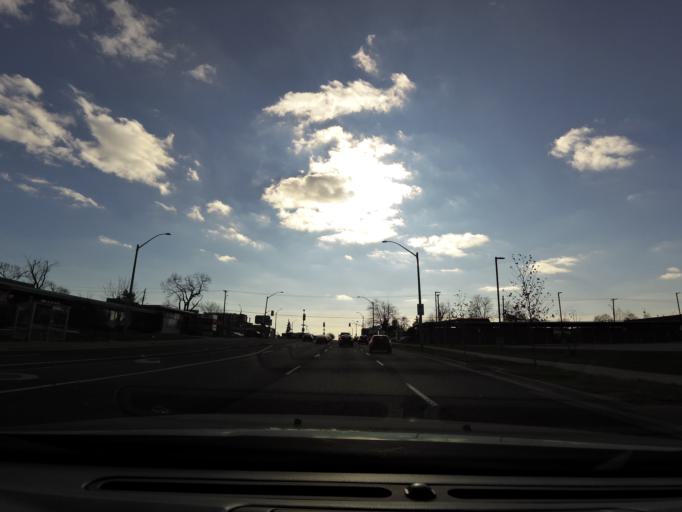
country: CA
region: Ontario
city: Hamilton
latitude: 43.2247
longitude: -79.8615
